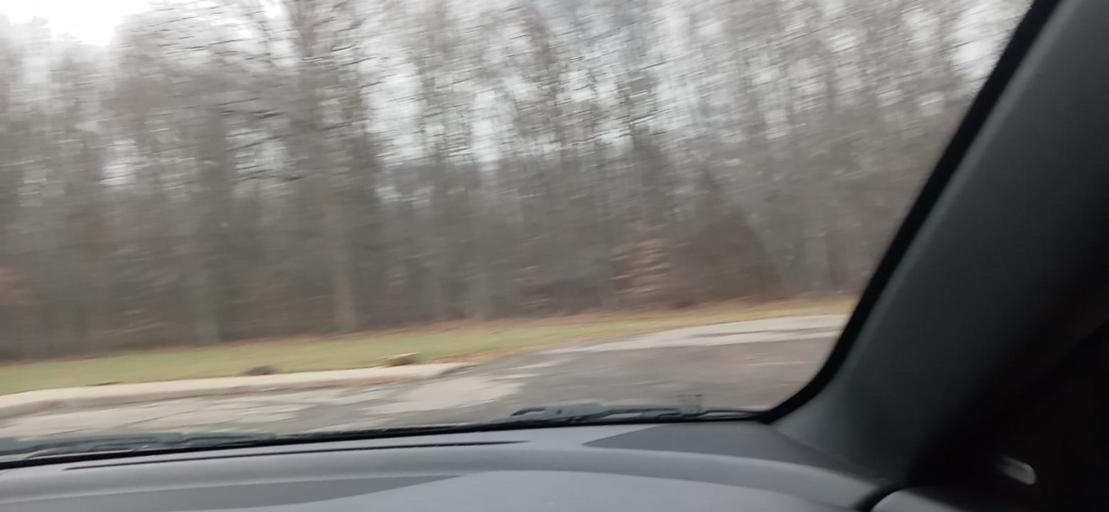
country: US
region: Ohio
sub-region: Trumbull County
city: Leavittsburg
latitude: 41.2326
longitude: -80.8891
